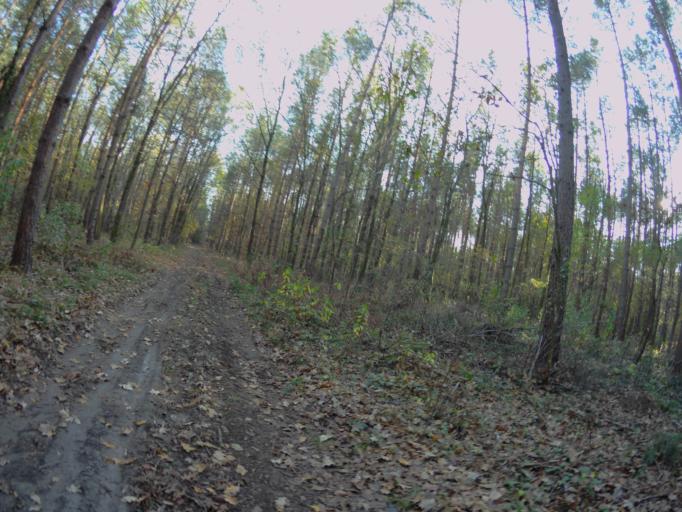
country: PL
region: Subcarpathian Voivodeship
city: Nowa Sarzyna
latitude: 50.3088
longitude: 22.3507
